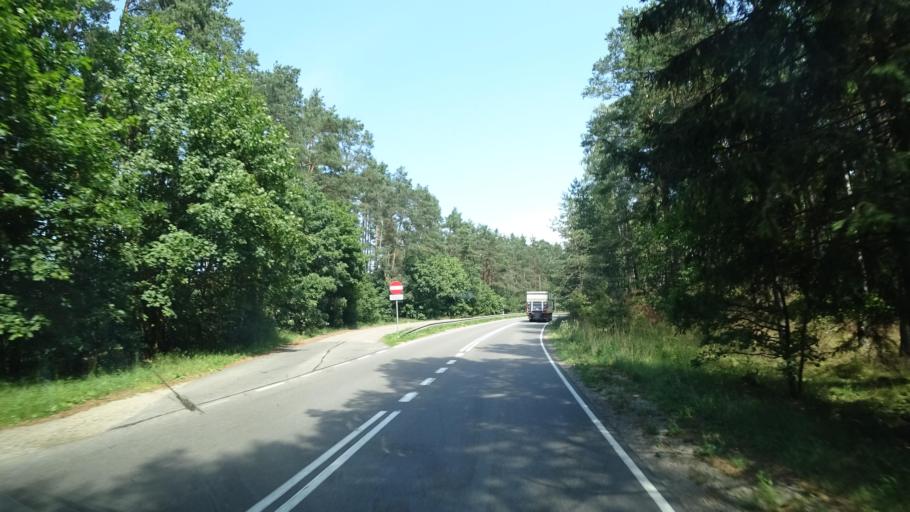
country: PL
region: Pomeranian Voivodeship
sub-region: Powiat koscierski
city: Lipusz
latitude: 54.0940
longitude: 17.8065
